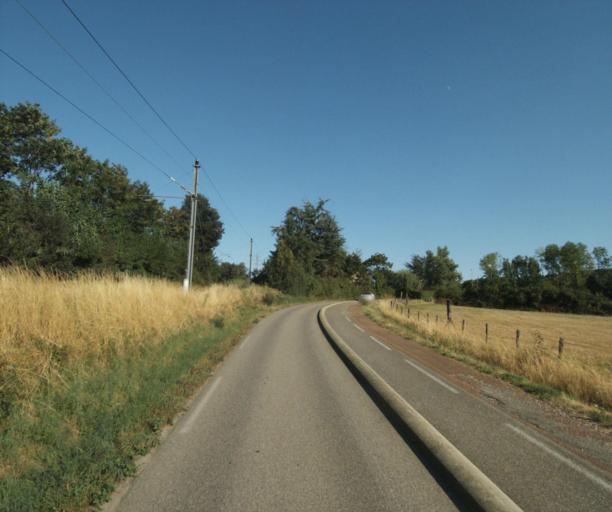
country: FR
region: Rhone-Alpes
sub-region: Departement du Rhone
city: Lentilly
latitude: 45.8184
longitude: 4.6718
